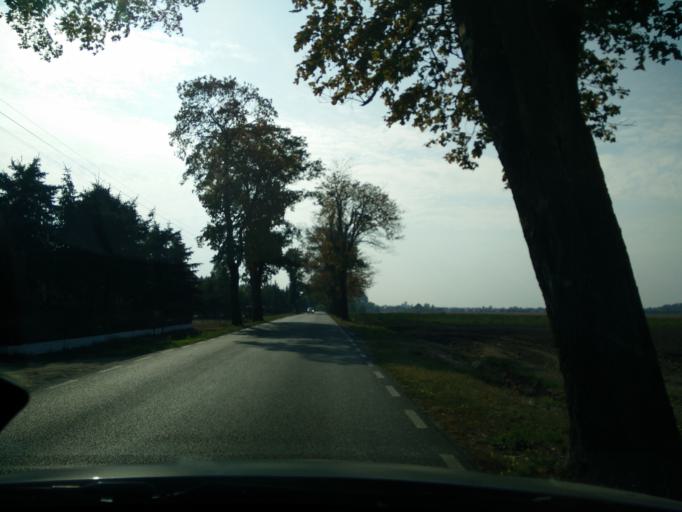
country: PL
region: Greater Poland Voivodeship
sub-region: Powiat sredzki
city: Sroda Wielkopolska
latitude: 52.2476
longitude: 17.2942
